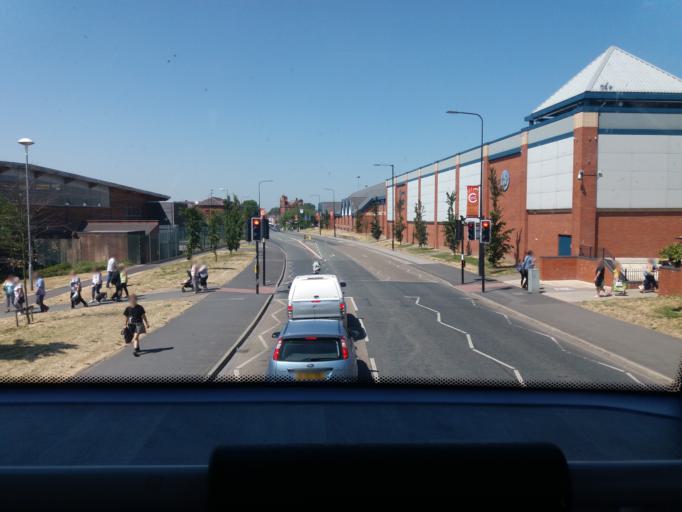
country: GB
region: England
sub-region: Borough of Wigan
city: Leigh
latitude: 53.4948
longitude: -2.5150
